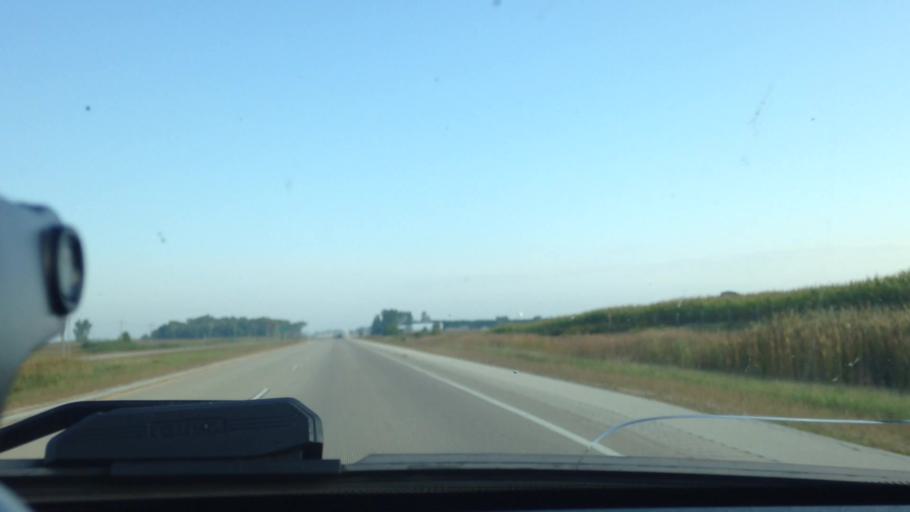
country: US
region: Wisconsin
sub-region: Oconto County
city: Oconto Falls
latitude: 45.0406
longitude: -88.0444
